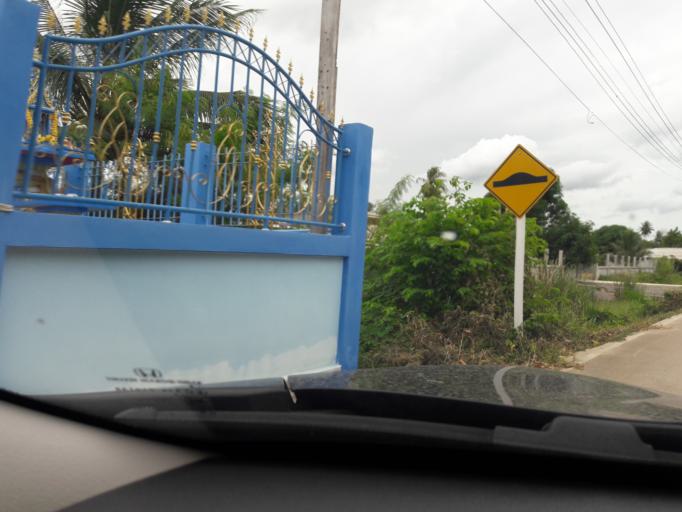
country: TH
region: Ratchaburi
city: Bang Phae
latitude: 13.6114
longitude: 99.9101
